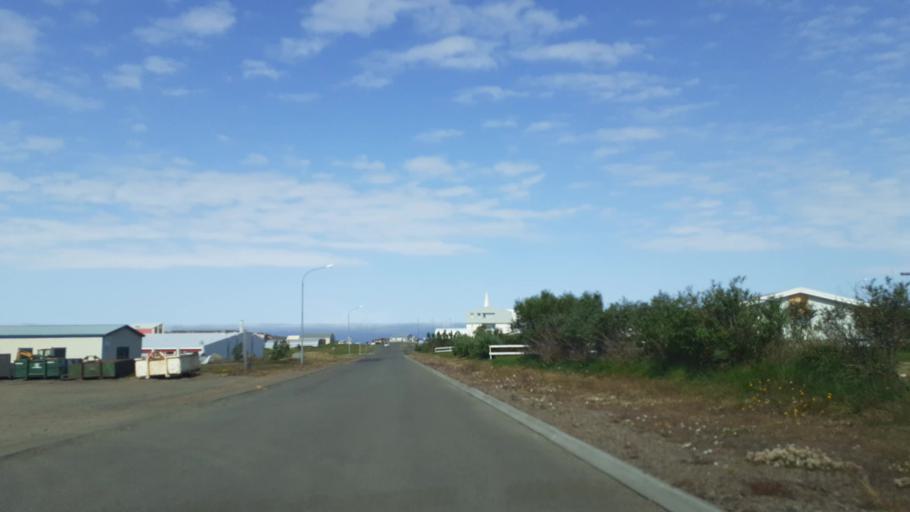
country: IS
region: Northwest
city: Saudarkrokur
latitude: 65.8205
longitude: -20.3020
